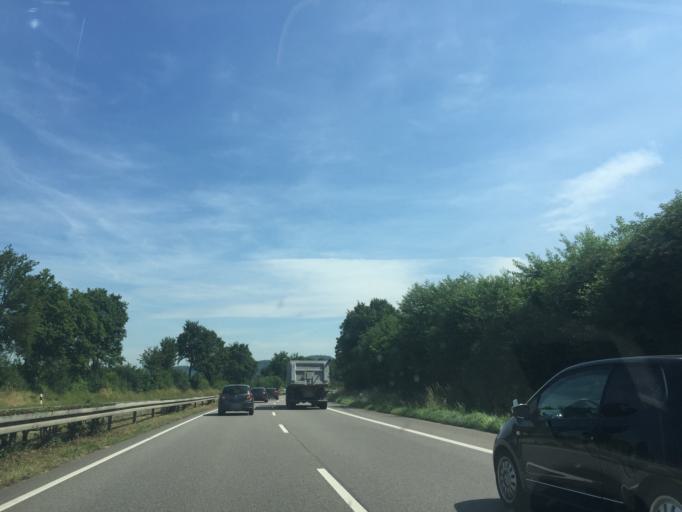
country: DE
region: Baden-Wuerttemberg
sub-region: Karlsruhe Region
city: Weinheim
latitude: 49.5541
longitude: 8.6422
